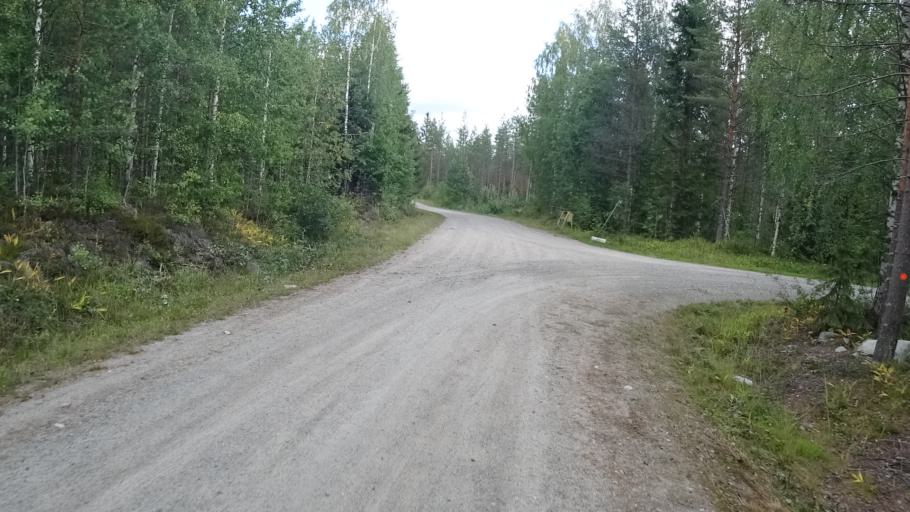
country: FI
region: North Karelia
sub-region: Joensuu
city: Ilomantsi
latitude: 62.6194
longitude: 31.2396
